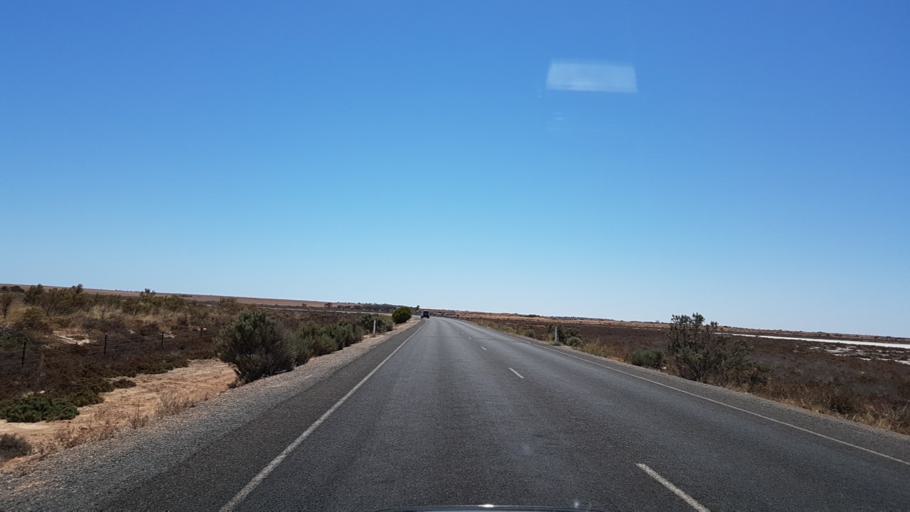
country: AU
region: South Australia
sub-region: Copper Coast
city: Wallaroo
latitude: -33.9176
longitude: 137.6461
